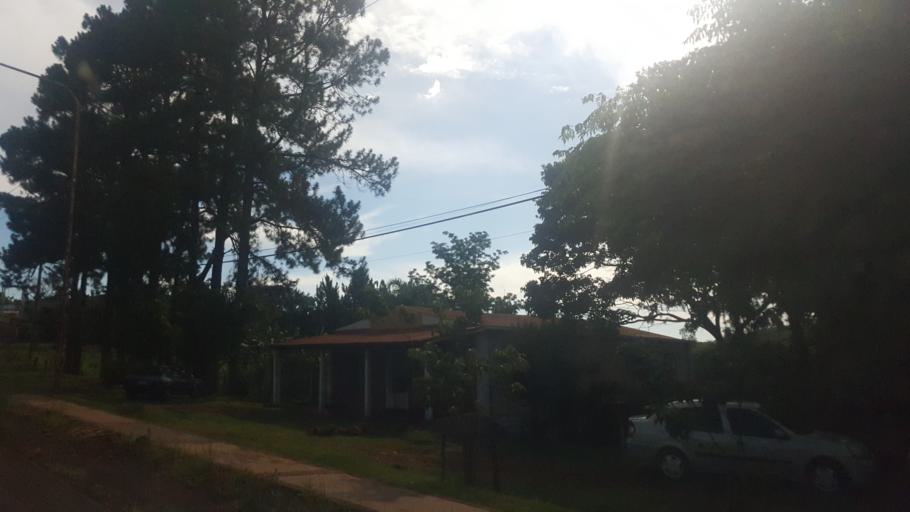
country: AR
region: Misiones
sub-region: Departamento de Leandro N. Alem
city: Leandro N. Alem
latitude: -27.5908
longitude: -55.3220
